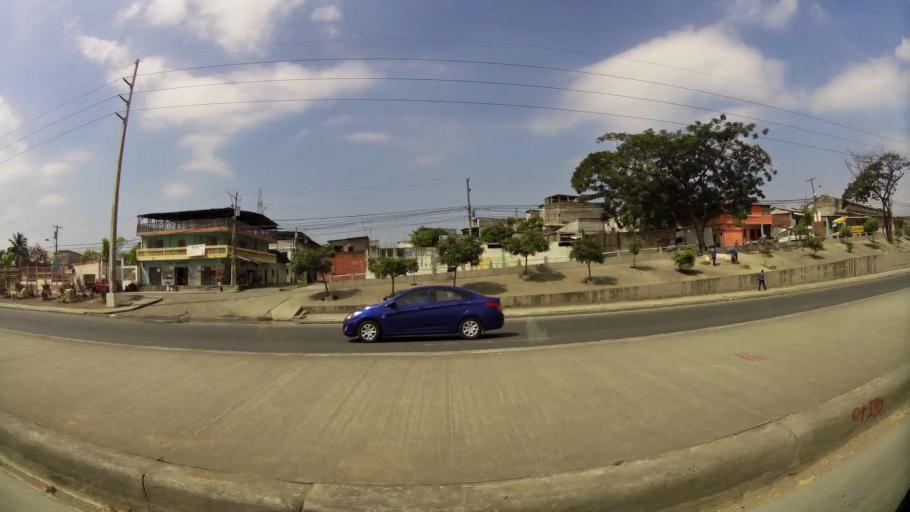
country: EC
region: Guayas
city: Eloy Alfaro
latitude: -2.0675
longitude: -79.9248
